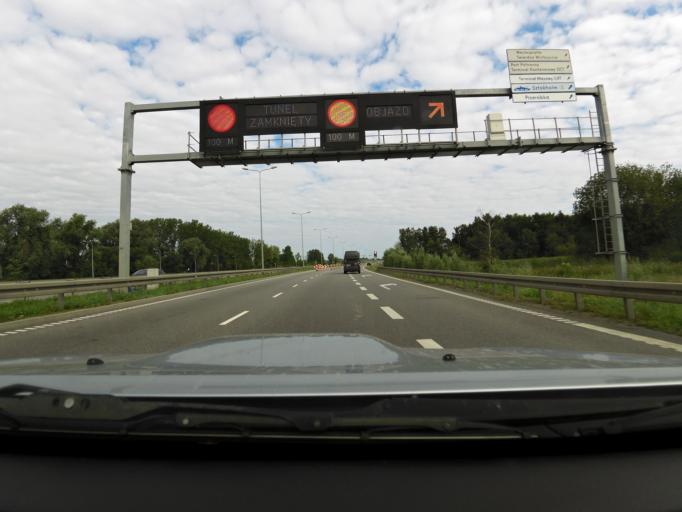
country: PL
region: Pomeranian Voivodeship
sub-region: Gdansk
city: Gdansk
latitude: 54.3707
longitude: 18.6850
